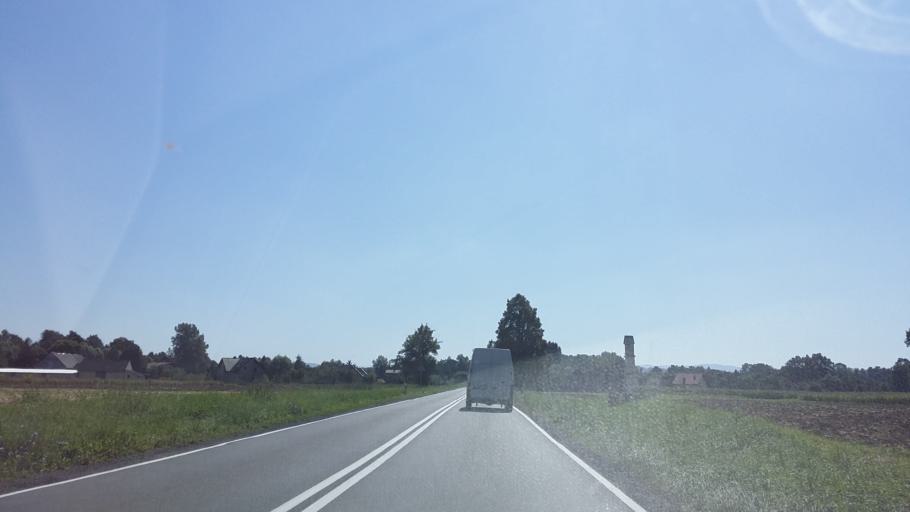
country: PL
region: Lesser Poland Voivodeship
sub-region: Powiat oswiecimski
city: Zator
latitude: 49.9657
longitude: 19.4407
